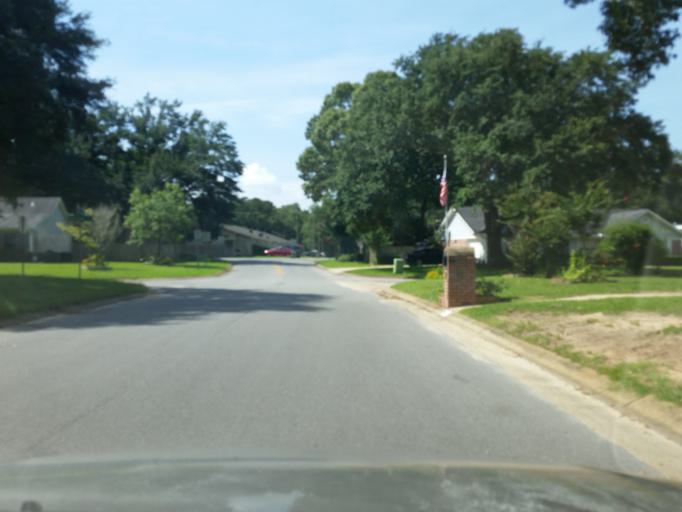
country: US
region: Florida
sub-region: Escambia County
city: Ferry Pass
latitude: 30.5181
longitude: -87.2062
